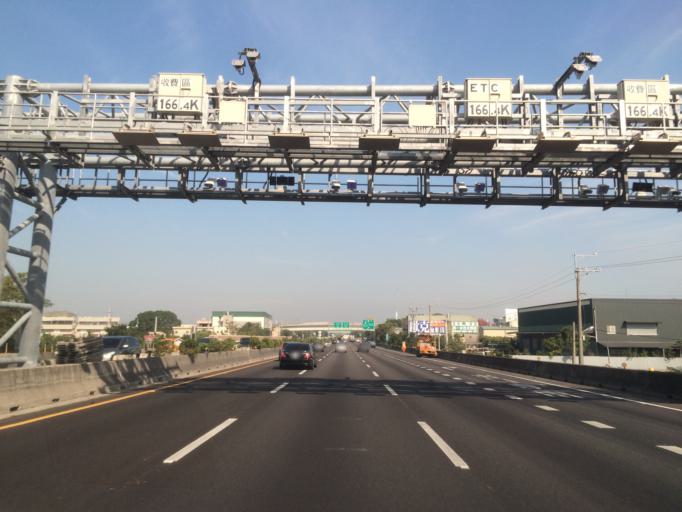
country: TW
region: Taiwan
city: Fengyuan
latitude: 24.2624
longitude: 120.6920
